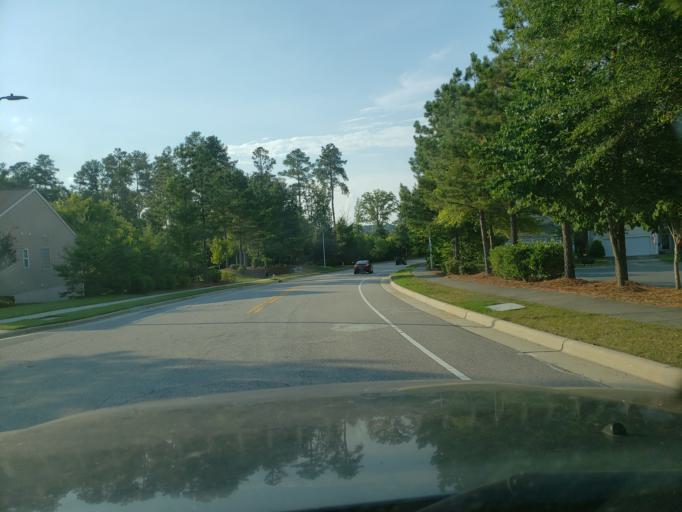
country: US
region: North Carolina
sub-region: Wake County
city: Green Level
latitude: 35.8334
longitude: -78.9149
